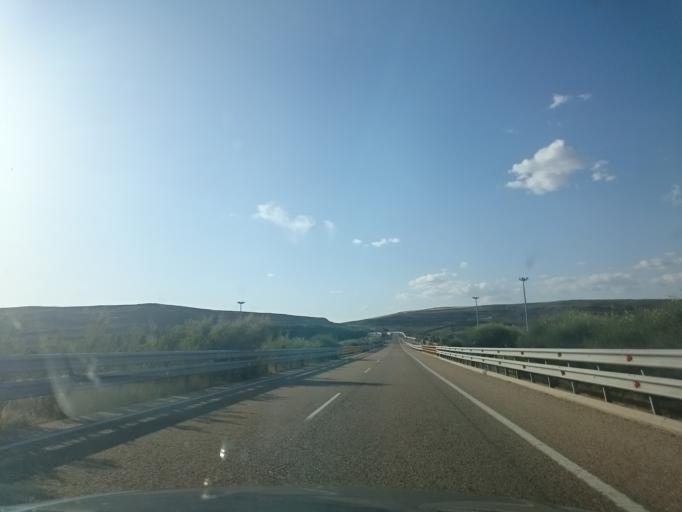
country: ES
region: Castille and Leon
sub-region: Provincia de Burgos
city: San Mames de Burgos
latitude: 42.3478
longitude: -3.7933
